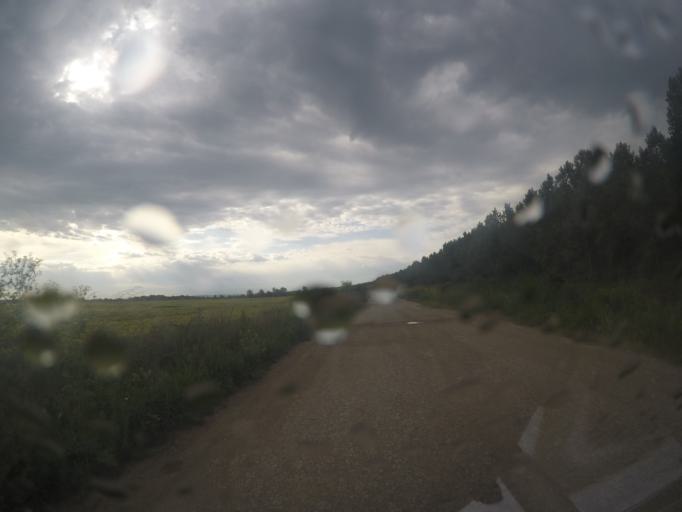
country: RS
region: Central Serbia
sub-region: Belgrade
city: Zemun
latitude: 44.8761
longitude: 20.3830
